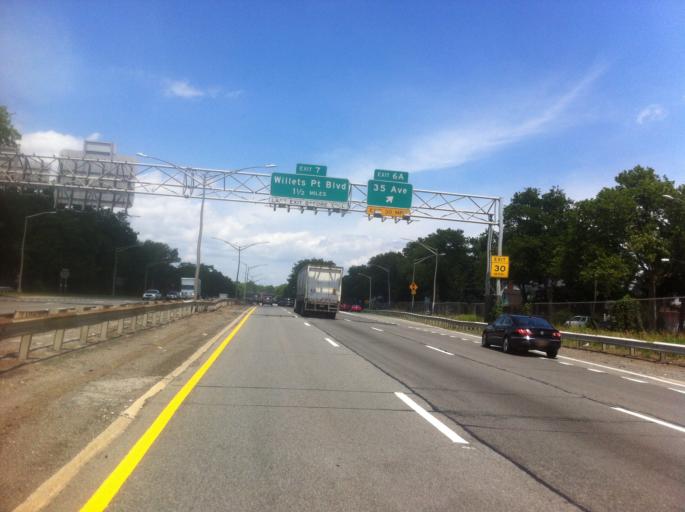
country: US
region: New York
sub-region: Nassau County
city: East Atlantic Beach
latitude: 40.7611
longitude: -73.7781
